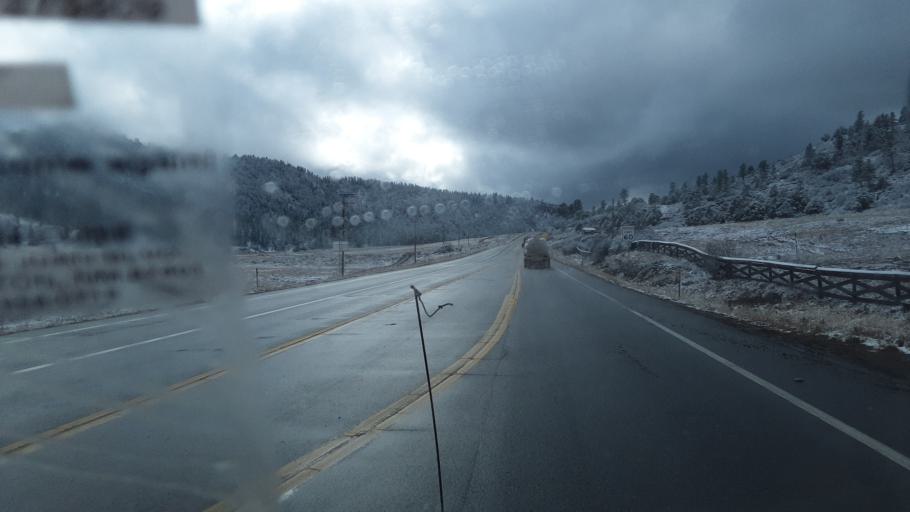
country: US
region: Colorado
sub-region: Archuleta County
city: Pagosa Springs
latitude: 37.2237
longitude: -107.2171
